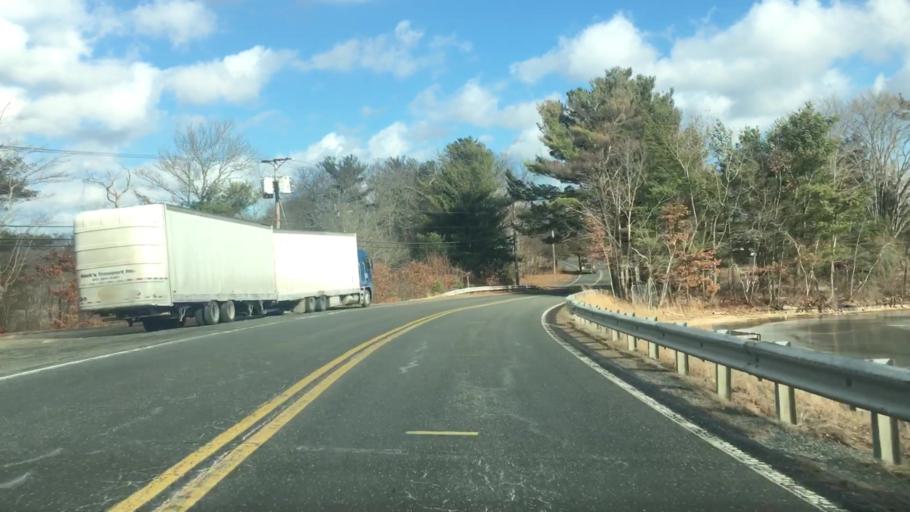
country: US
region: Massachusetts
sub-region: Hampden County
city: Wales
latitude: 42.0633
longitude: -72.2249
